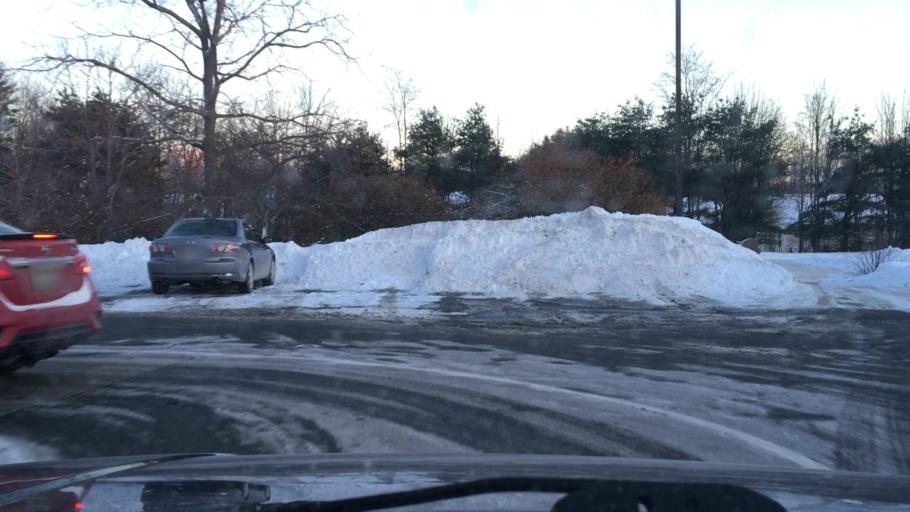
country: US
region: Maine
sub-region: York County
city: Saco
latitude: 43.5085
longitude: -70.4349
